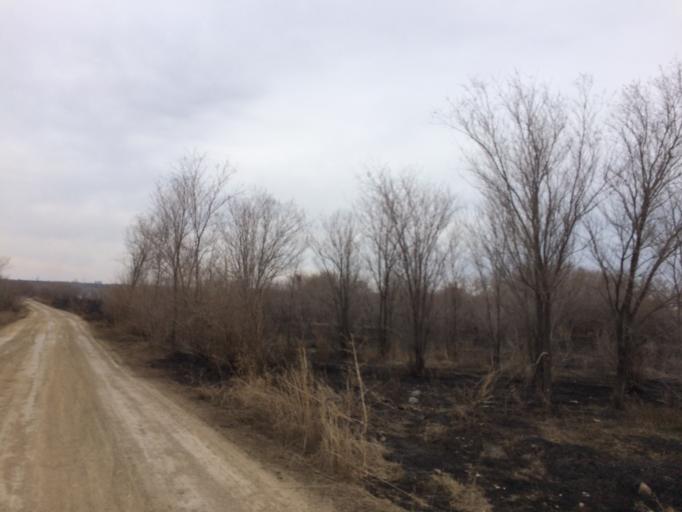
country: RU
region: Chelyabinsk
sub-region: Gorod Magnitogorsk
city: Magnitogorsk
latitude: 53.4410
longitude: 58.9767
